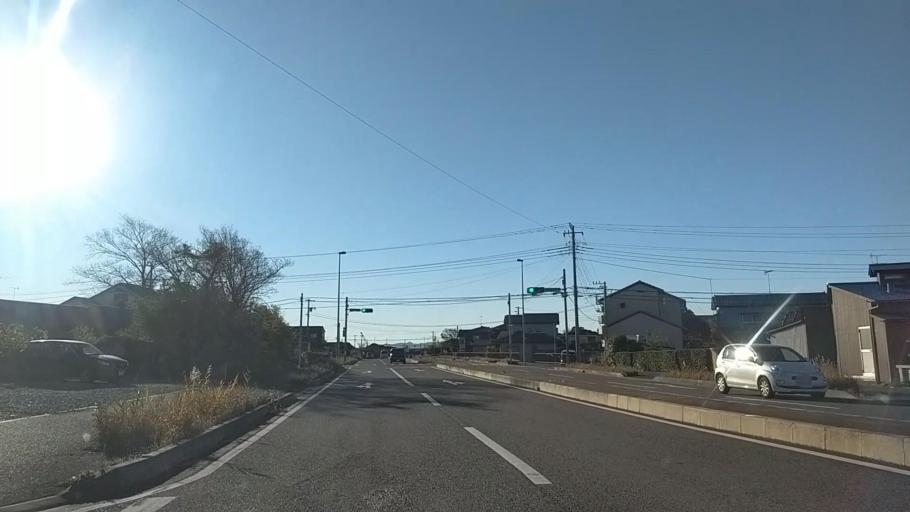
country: JP
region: Chiba
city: Kisarazu
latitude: 35.4023
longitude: 139.9199
